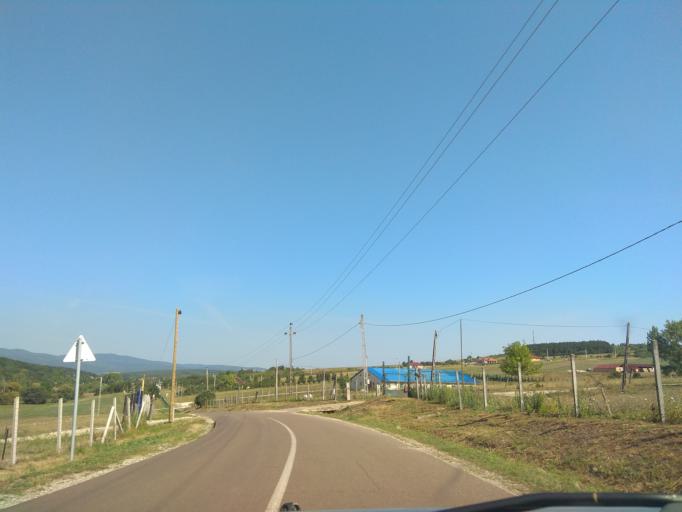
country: HU
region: Borsod-Abauj-Zemplen
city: Nyekladhaza
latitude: 47.9752
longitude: 20.7942
